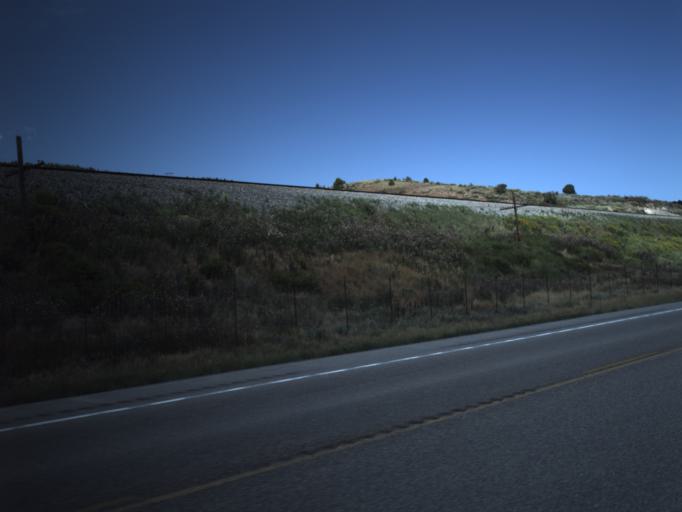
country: US
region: Utah
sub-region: Carbon County
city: Helper
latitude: 39.8964
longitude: -111.0541
